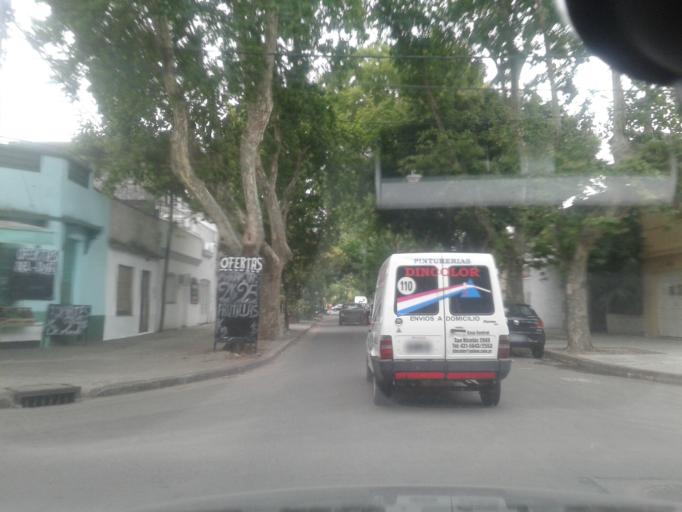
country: AR
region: Santa Fe
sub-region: Departamento de Rosario
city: Rosario
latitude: -32.9496
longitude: -60.6775
